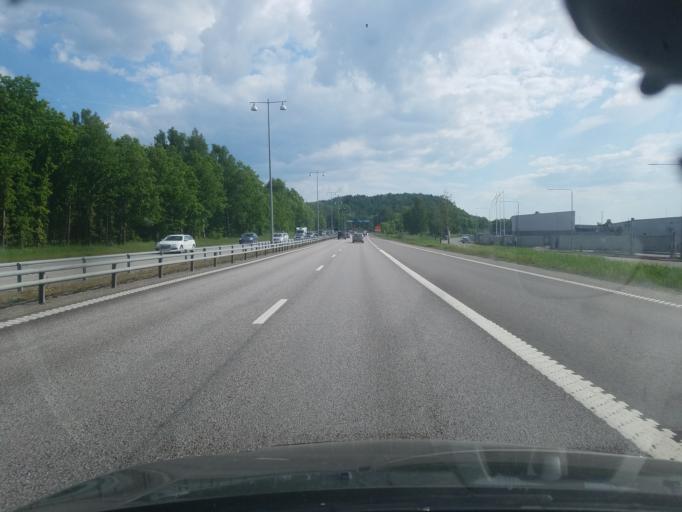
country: SE
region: Vaestra Goetaland
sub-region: Goteborg
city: Gardsten
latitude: 57.7930
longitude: 12.0155
